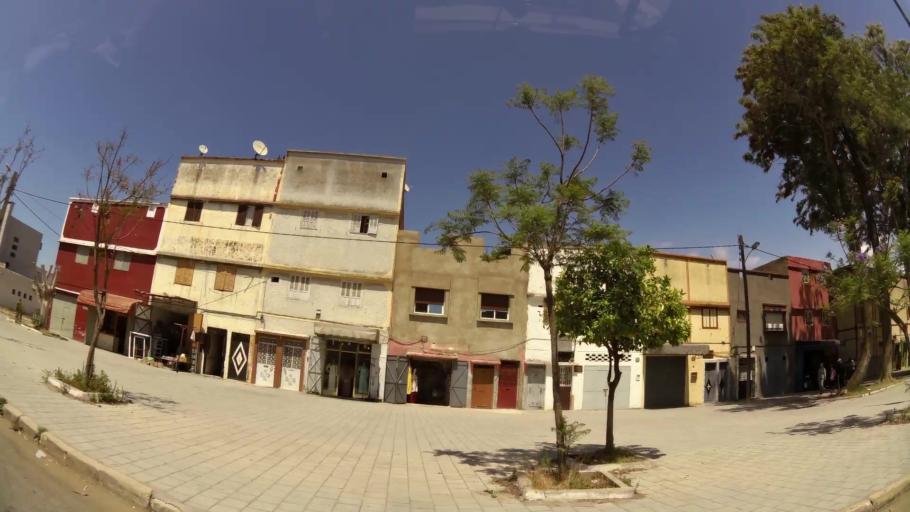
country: MA
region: Gharb-Chrarda-Beni Hssen
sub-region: Kenitra Province
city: Kenitra
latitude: 34.2498
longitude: -6.5455
